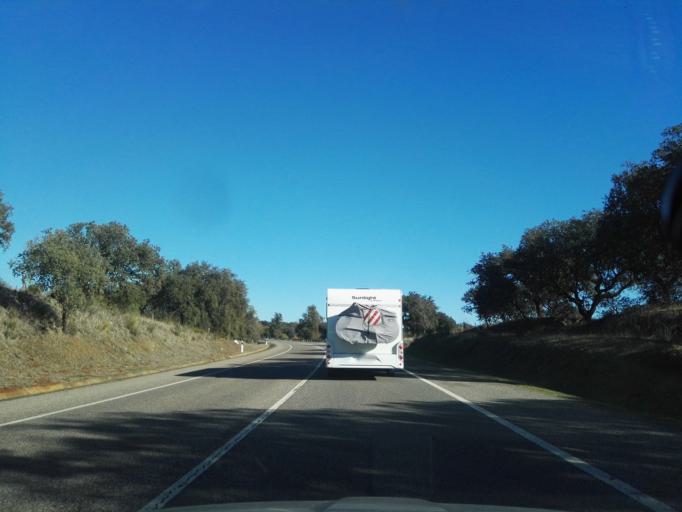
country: PT
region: Evora
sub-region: Vila Vicosa
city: Vila Vicosa
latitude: 38.8540
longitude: -7.3224
